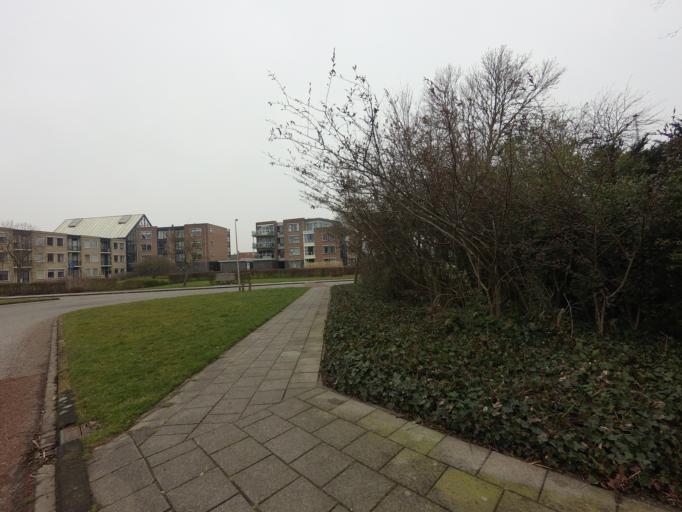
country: NL
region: Friesland
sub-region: Gemeente Franekeradeel
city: Franeker
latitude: 53.1859
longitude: 5.5548
